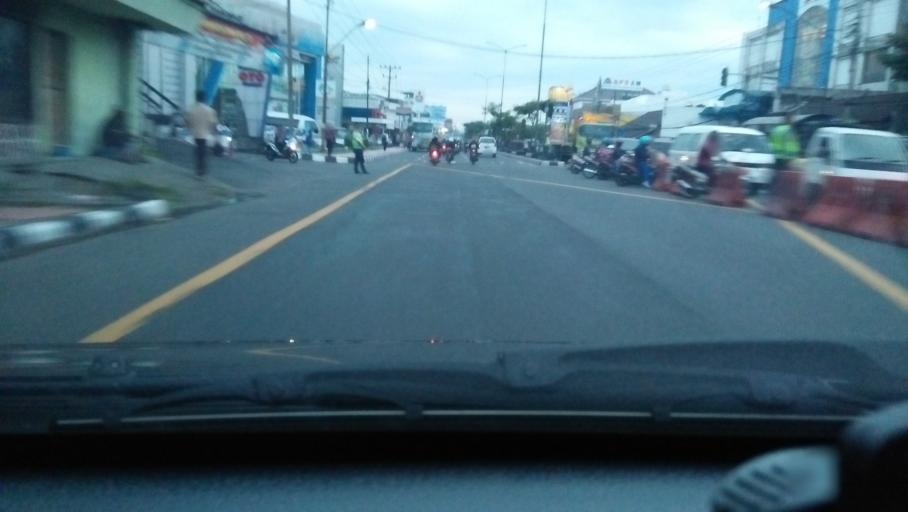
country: ID
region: Central Java
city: Mertoyudan
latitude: -7.5049
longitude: 110.2240
